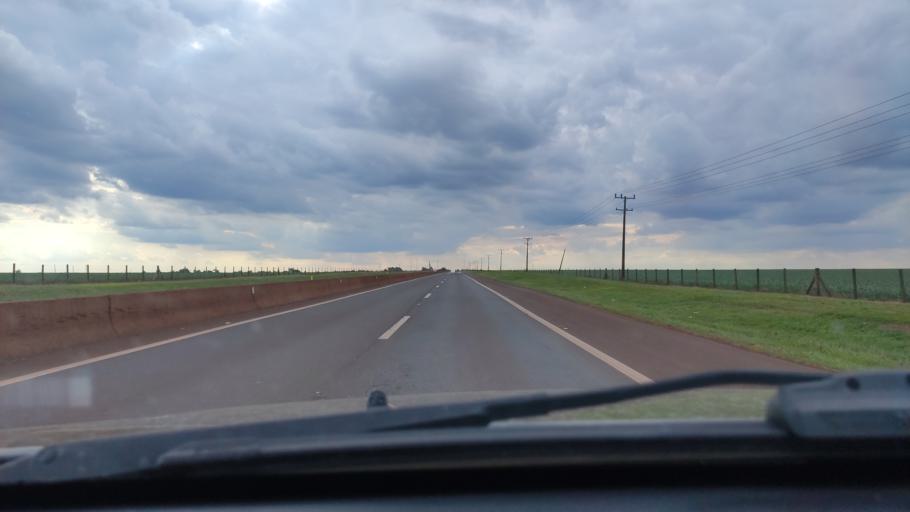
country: BR
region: Sao Paulo
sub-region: Palmital
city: Palmital
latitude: -22.8216
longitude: -50.0419
